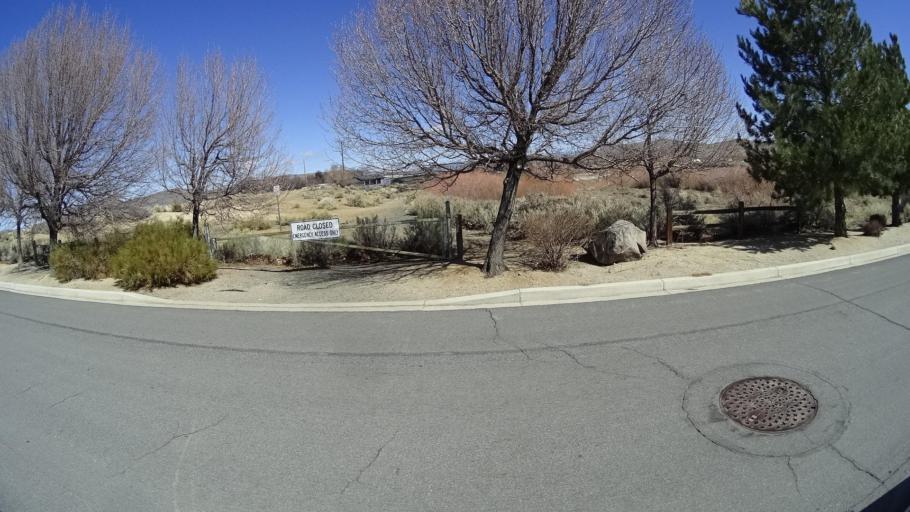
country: US
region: Nevada
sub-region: Washoe County
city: Lemmon Valley
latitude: 39.6351
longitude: -119.8669
